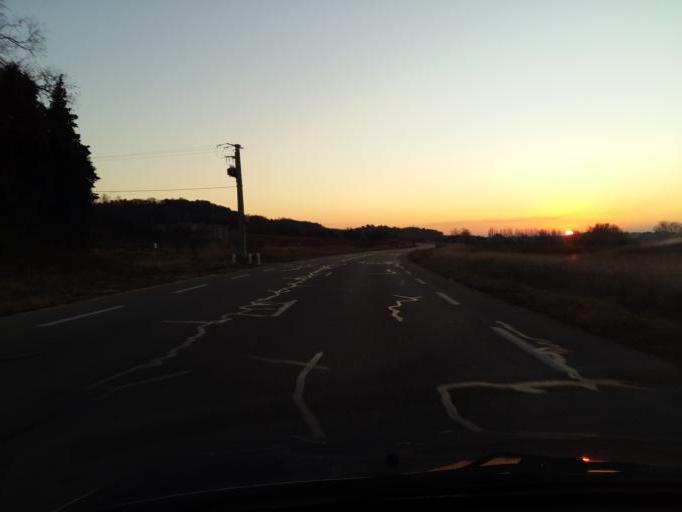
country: FR
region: Provence-Alpes-Cote d'Azur
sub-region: Departement du Vaucluse
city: Valreas
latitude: 44.3567
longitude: 4.9680
